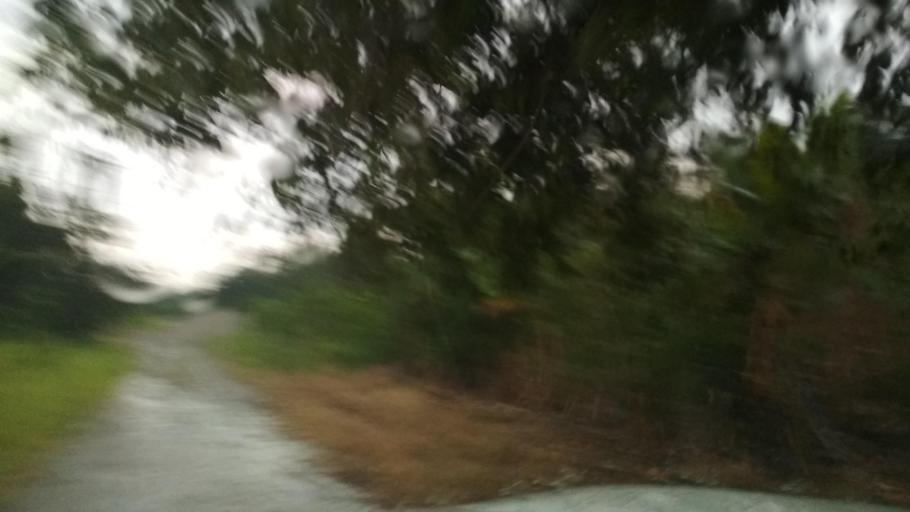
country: MM
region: Shan
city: Taunggyi
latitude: 20.3008
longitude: 97.3022
